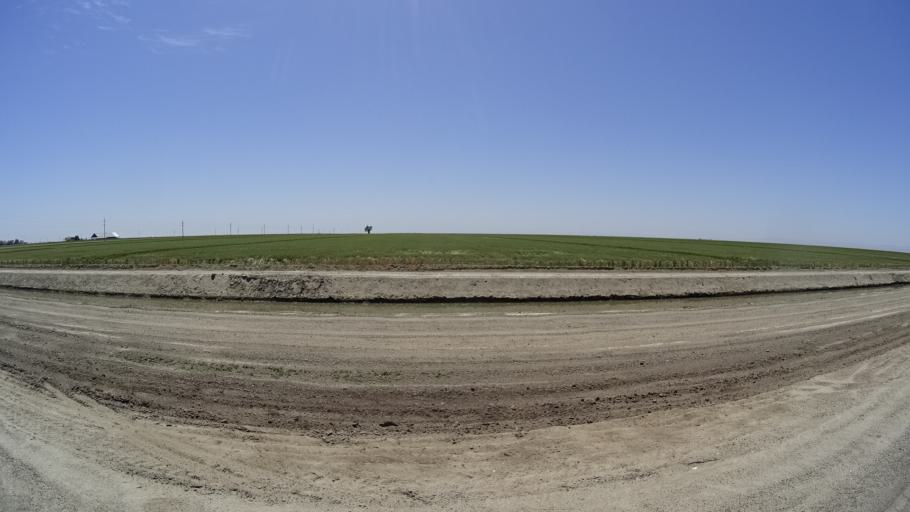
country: US
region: California
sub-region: Kings County
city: Corcoran
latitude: 36.1163
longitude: -119.6467
